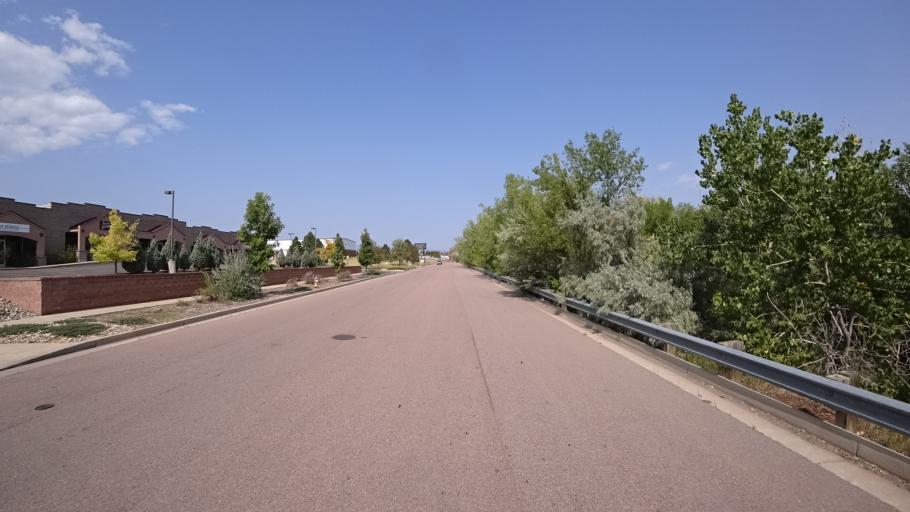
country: US
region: Colorado
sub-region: El Paso County
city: Cimarron Hills
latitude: 38.8373
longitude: -104.7406
